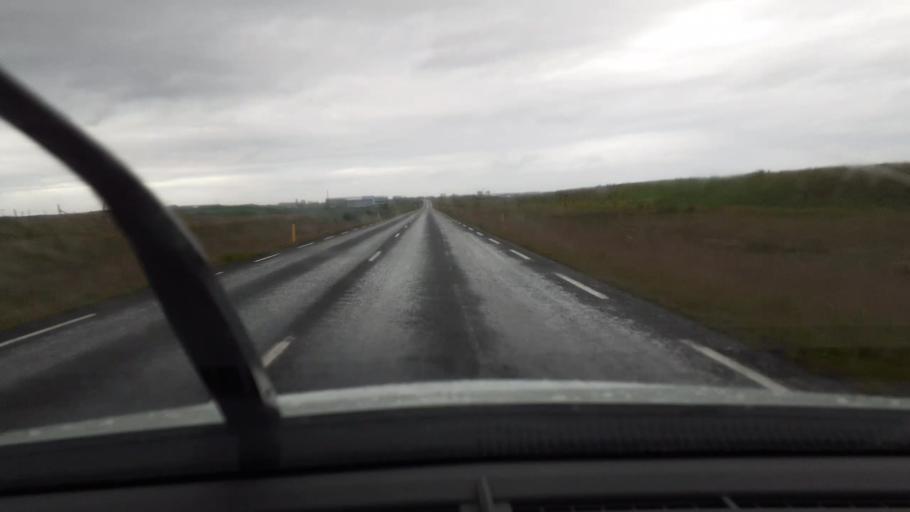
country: IS
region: West
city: Akranes
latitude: 64.3470
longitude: -22.0055
